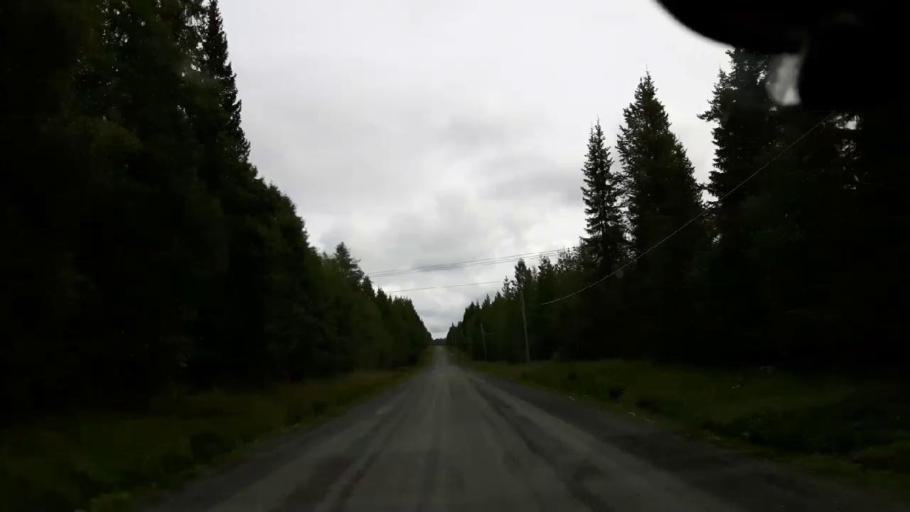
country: SE
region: Jaemtland
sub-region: Krokoms Kommun
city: Valla
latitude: 63.6882
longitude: 13.8932
